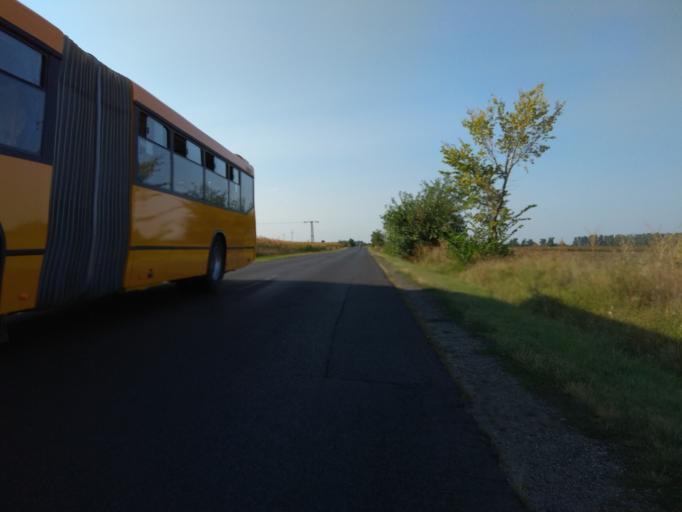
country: HU
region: Borsod-Abauj-Zemplen
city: Onod
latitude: 48.0146
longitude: 20.9079
